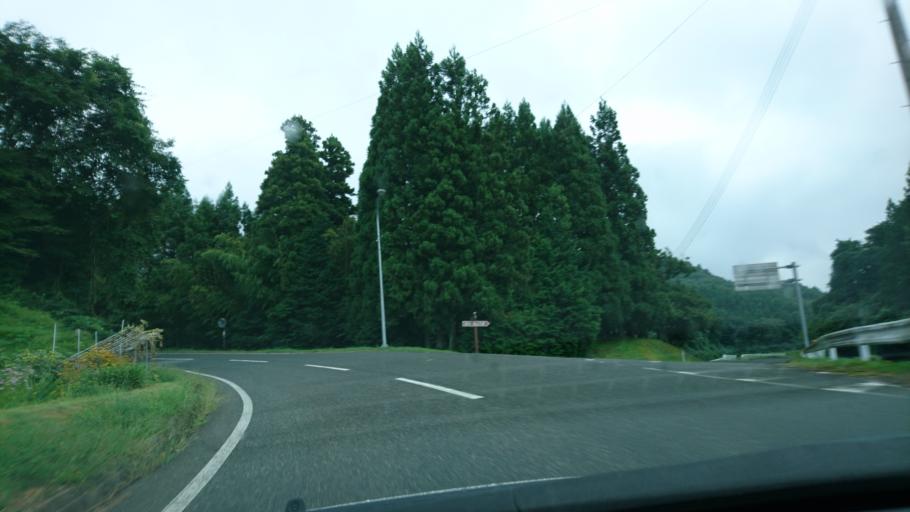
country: JP
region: Iwate
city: Ichinoseki
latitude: 38.8831
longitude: 140.9742
